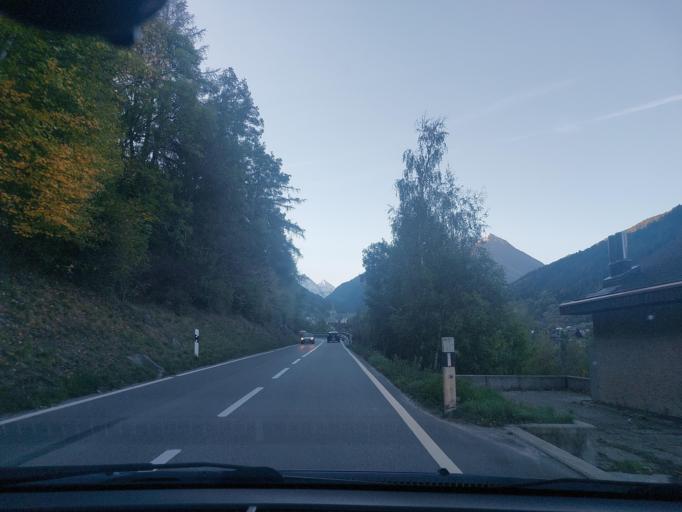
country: CH
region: Valais
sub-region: Sierre District
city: Chippis
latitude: 46.2203
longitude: 7.5828
